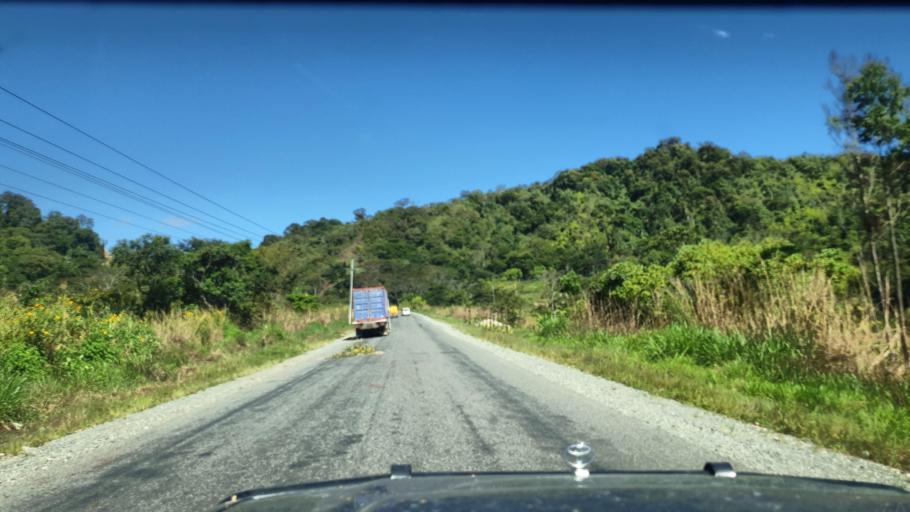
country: PG
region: Western Highlands
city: Rauna
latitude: -5.8251
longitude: 144.3780
